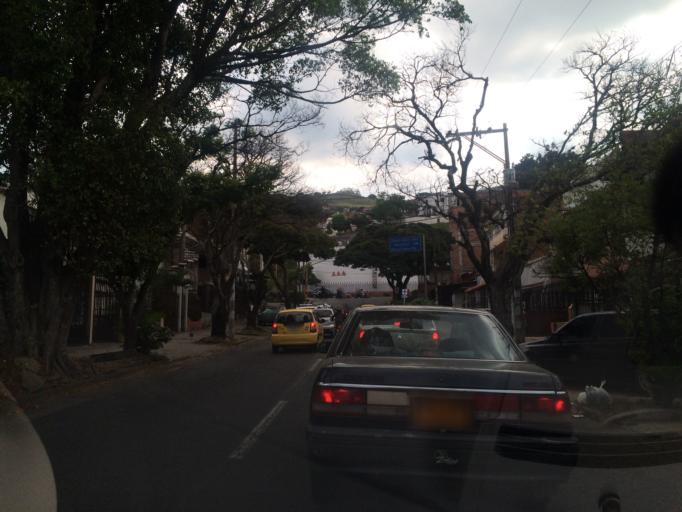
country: CO
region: Valle del Cauca
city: Cali
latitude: 3.4253
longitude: -76.5515
